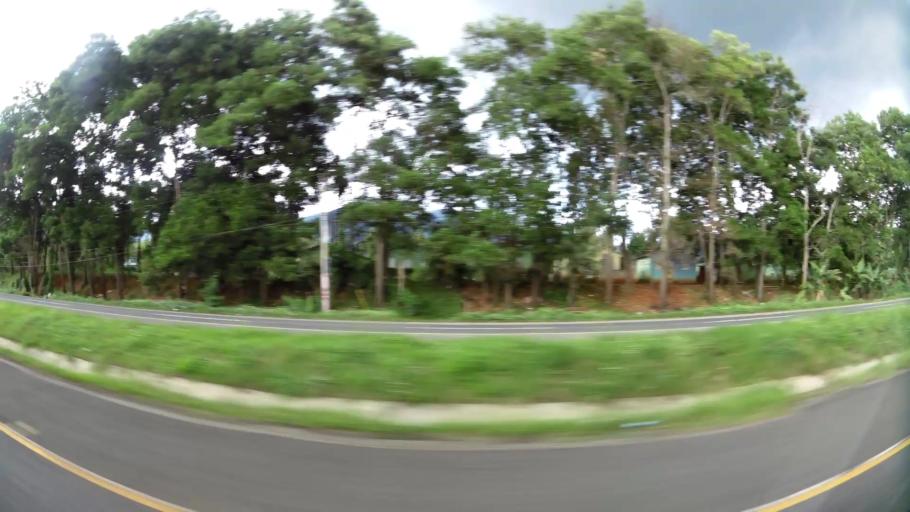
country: DO
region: San Cristobal
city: Villa Altagracia
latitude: 18.7528
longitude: -70.2349
